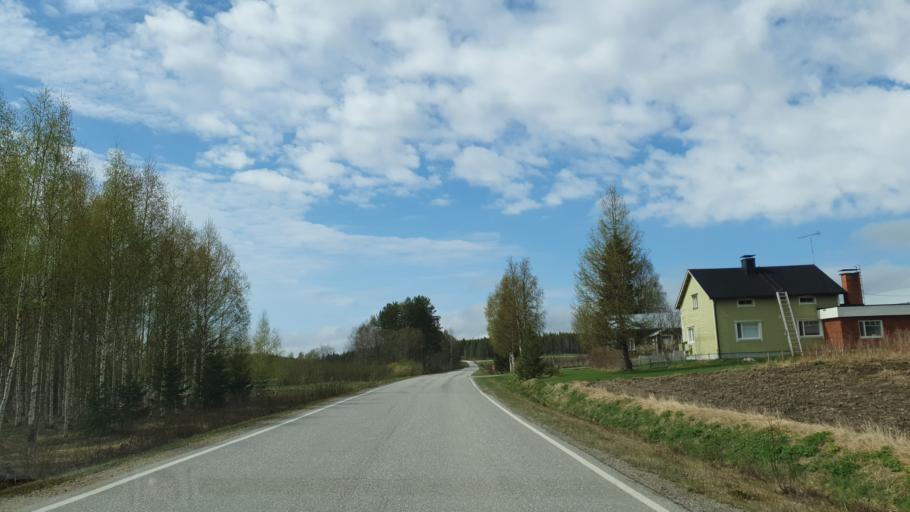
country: FI
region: Kainuu
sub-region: Kehys-Kainuu
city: Kuhmo
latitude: 64.1182
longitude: 29.7011
